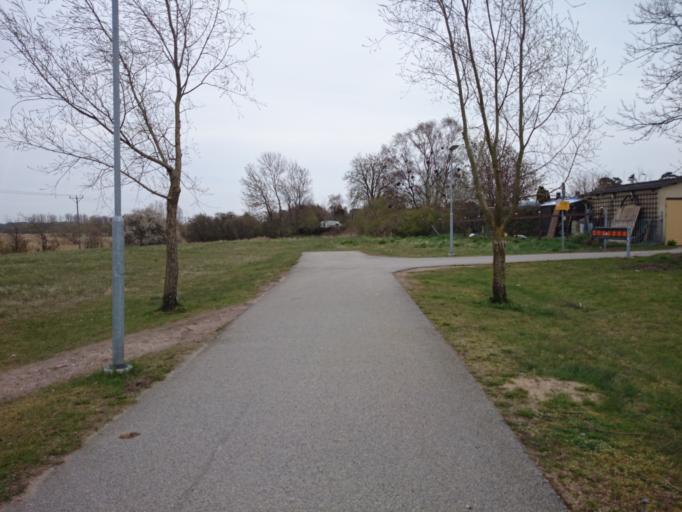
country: SE
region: Skane
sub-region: Landskrona
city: Asmundtorp
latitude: 55.8574
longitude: 12.9107
